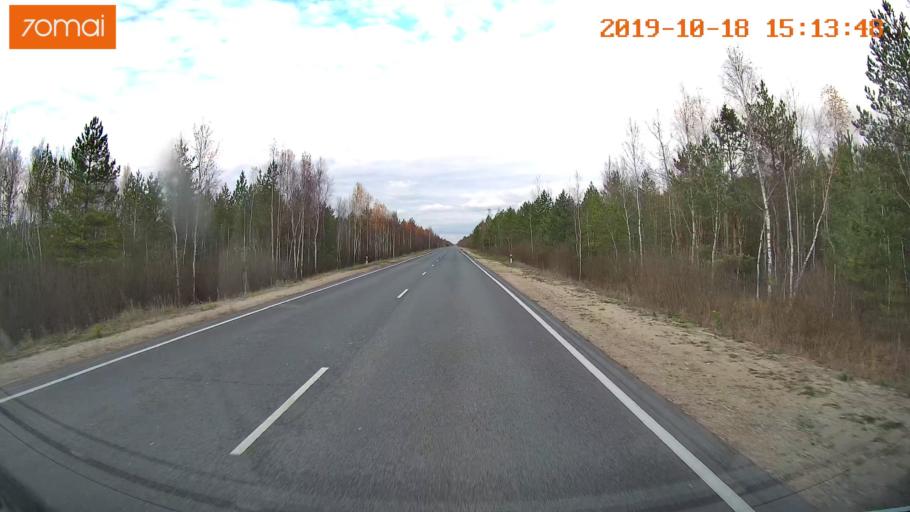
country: RU
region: Vladimir
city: Gus'-Khrustal'nyy
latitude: 55.5924
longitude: 40.7189
